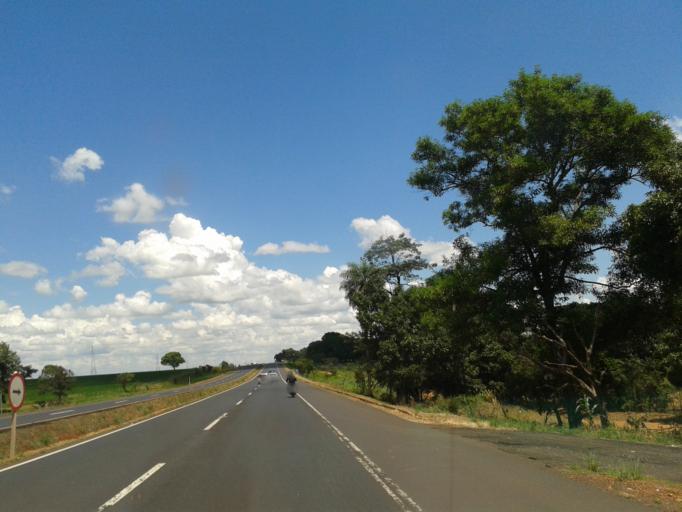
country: BR
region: Minas Gerais
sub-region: Centralina
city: Centralina
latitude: -18.6944
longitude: -49.1474
